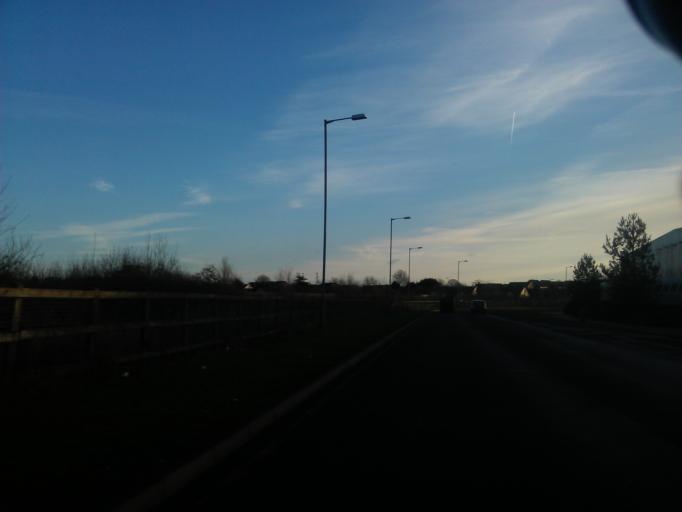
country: GB
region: England
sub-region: Essex
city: Little Clacton
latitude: 51.8128
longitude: 1.1486
